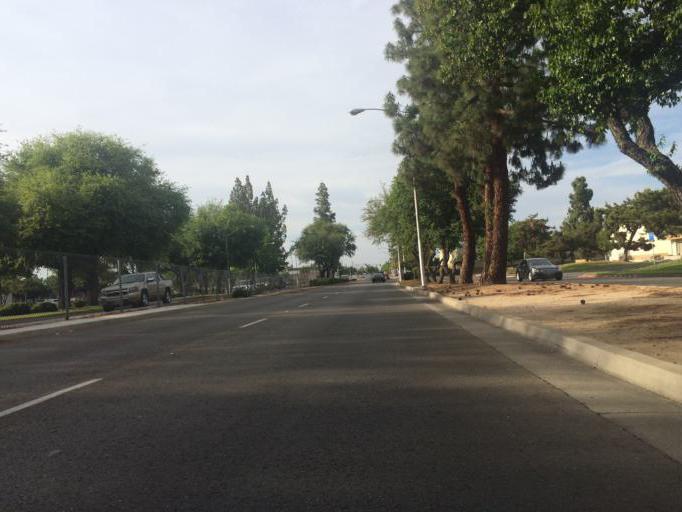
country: US
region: California
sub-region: Fresno County
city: Fresno
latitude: 36.8055
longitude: -119.7723
